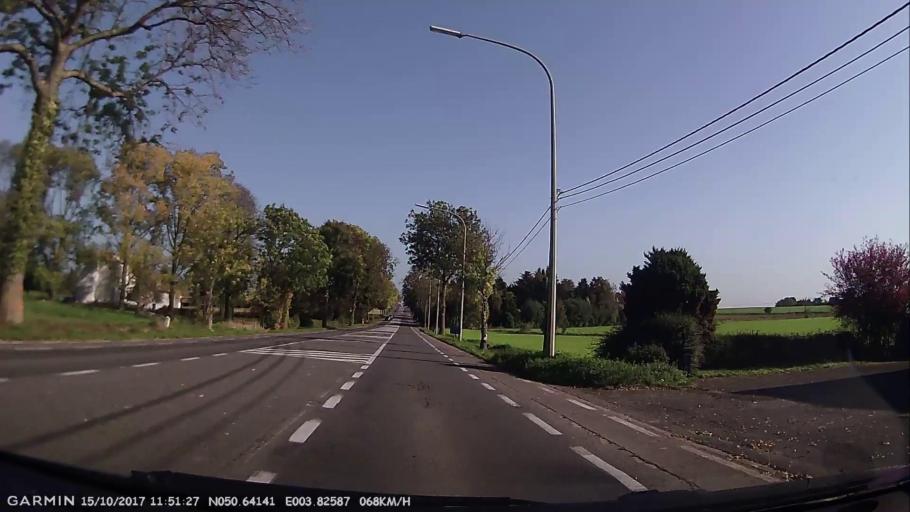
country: BE
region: Wallonia
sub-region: Province du Hainaut
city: Ath
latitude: 50.6415
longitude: 3.8261
